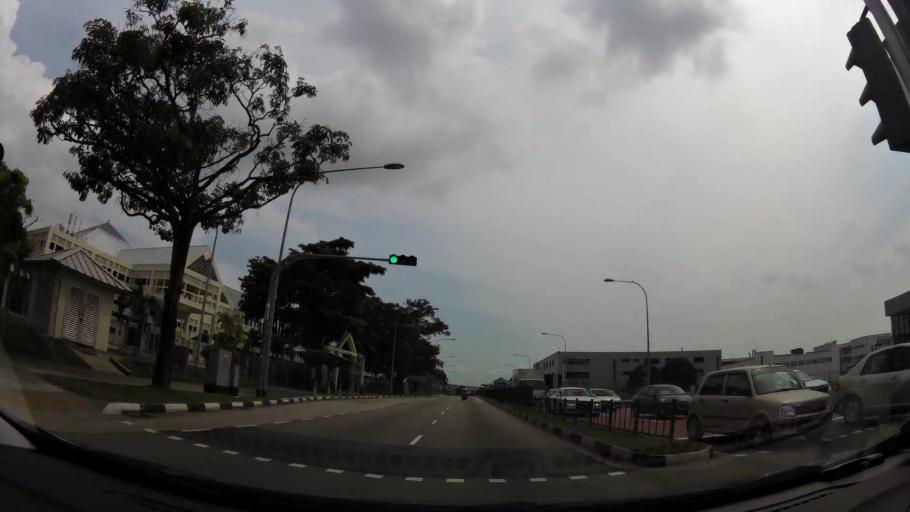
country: SG
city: Singapore
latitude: 1.3532
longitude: 103.9657
